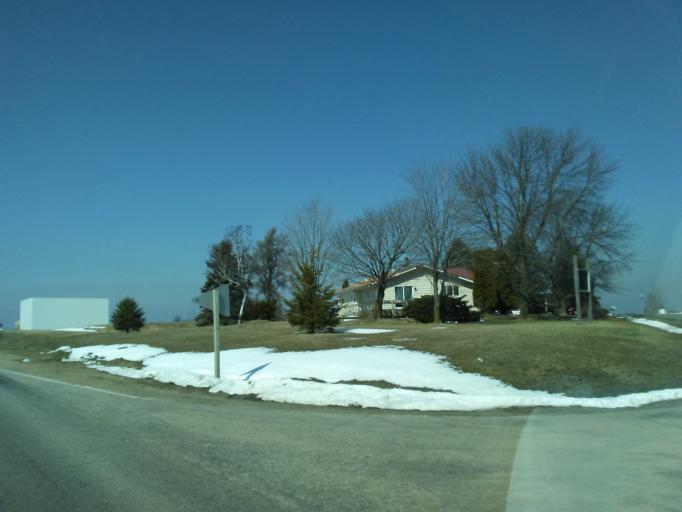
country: US
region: Wisconsin
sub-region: Vernon County
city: Westby
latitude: 43.6615
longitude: -90.8610
